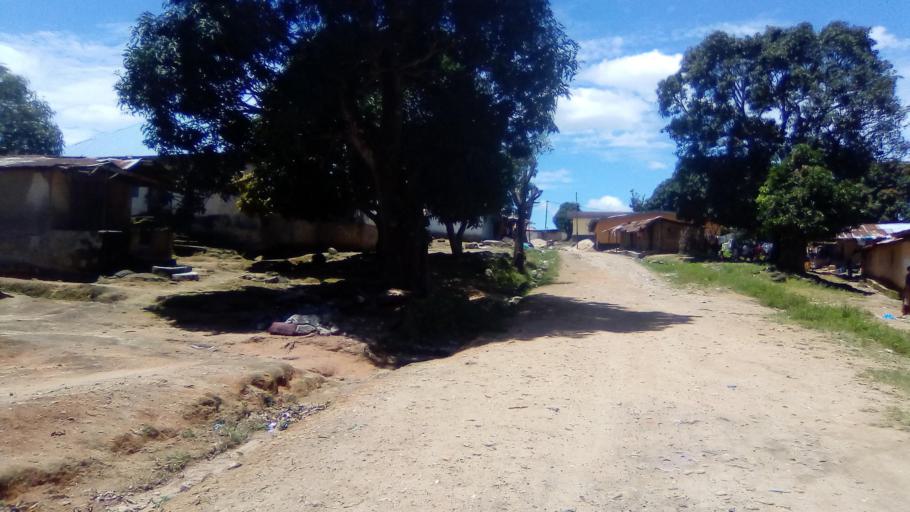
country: SL
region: Eastern Province
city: Simbakoro
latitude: 8.6252
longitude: -10.9898
